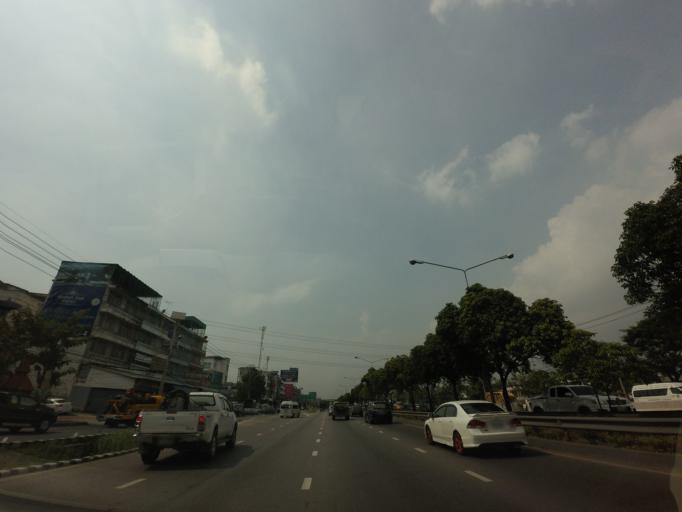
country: TH
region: Bangkok
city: Thawi Watthana
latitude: 13.7872
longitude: 100.3672
